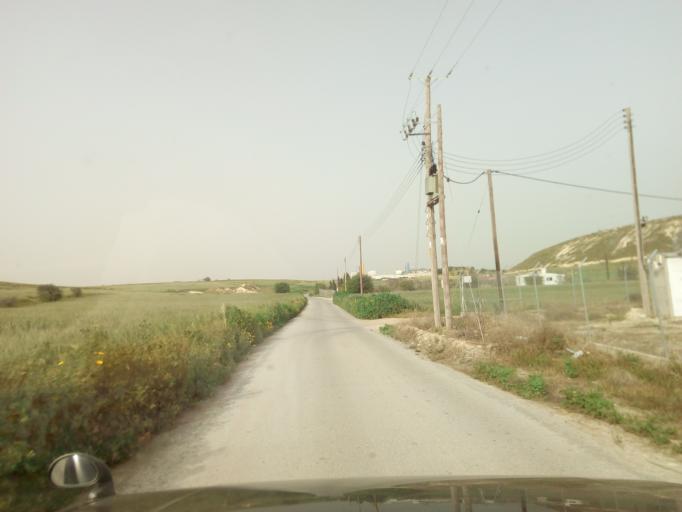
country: CY
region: Larnaka
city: Athienou
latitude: 35.0391
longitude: 33.5309
